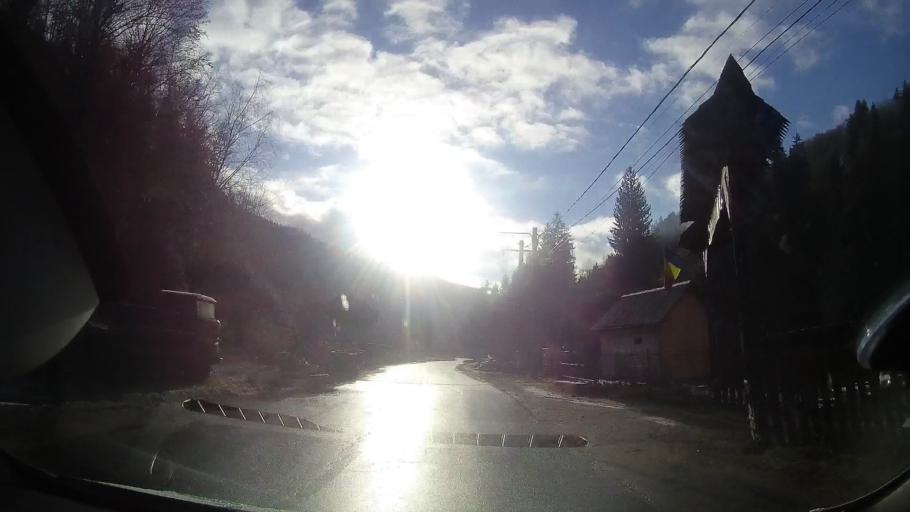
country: RO
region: Alba
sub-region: Comuna Albac
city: Albac
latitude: 46.4454
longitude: 22.9648
